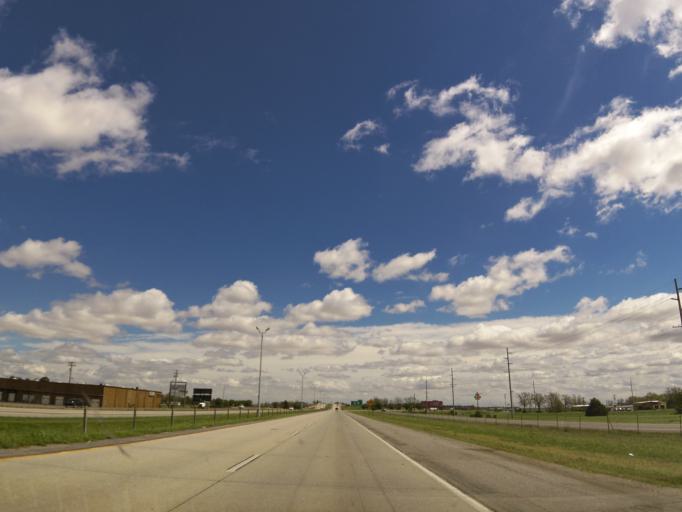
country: US
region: Arkansas
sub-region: Craighead County
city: Jonesboro
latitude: 35.8069
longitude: -90.6459
